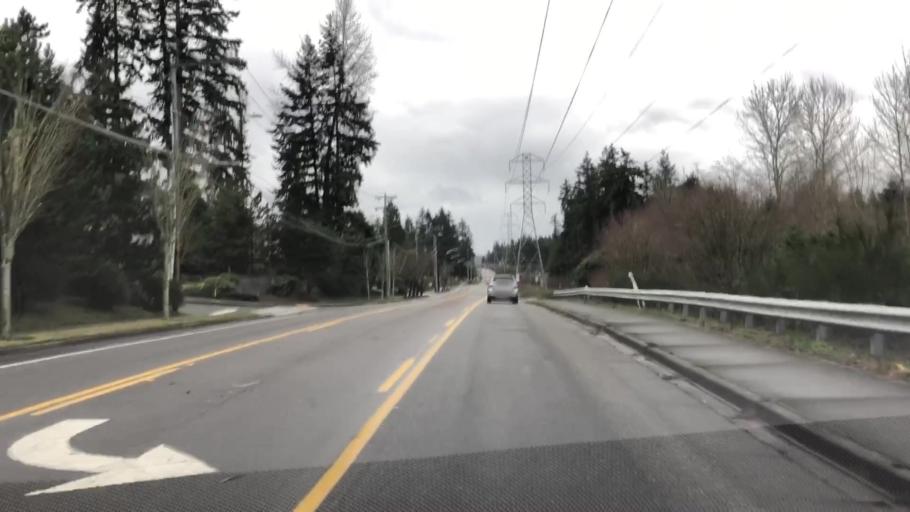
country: US
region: Washington
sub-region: King County
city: Kingsgate
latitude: 47.7410
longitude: -122.1752
